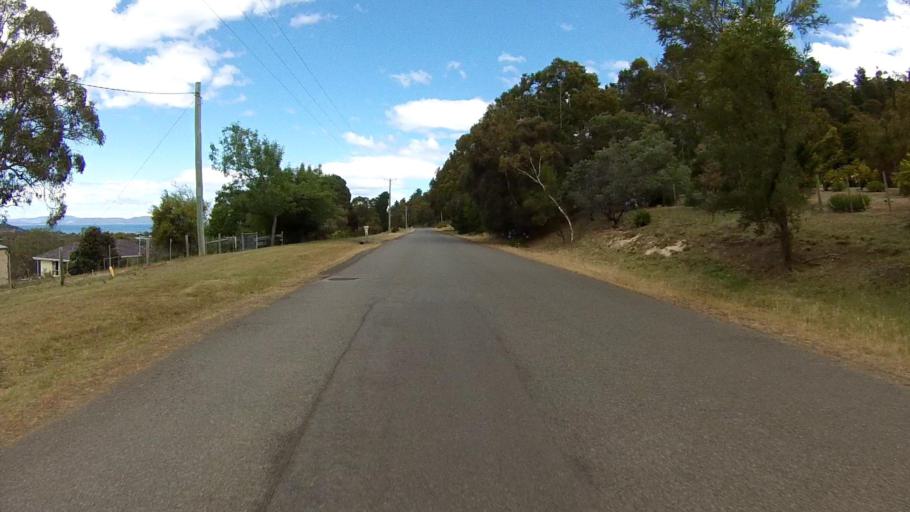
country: AU
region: Tasmania
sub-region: Clarence
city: Acton Park
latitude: -42.8656
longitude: 147.4699
